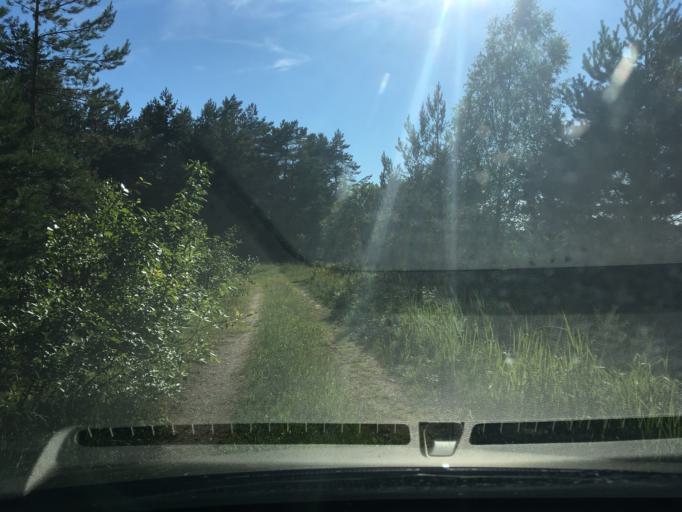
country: EE
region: Laeaene
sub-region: Lihula vald
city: Lihula
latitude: 58.5888
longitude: 23.7384
